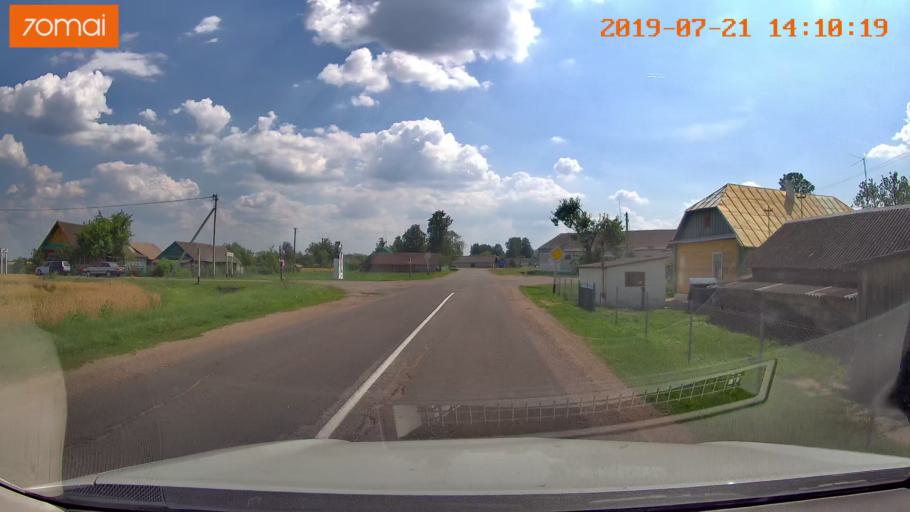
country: BY
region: Grodnenskaya
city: Karelichy
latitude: 53.6644
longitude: 26.1352
